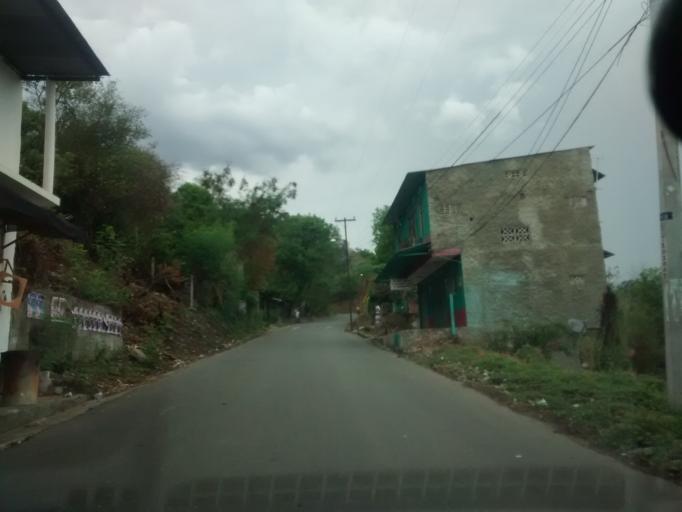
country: CO
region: Cundinamarca
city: Tocaima
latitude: 4.4577
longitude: -74.6399
